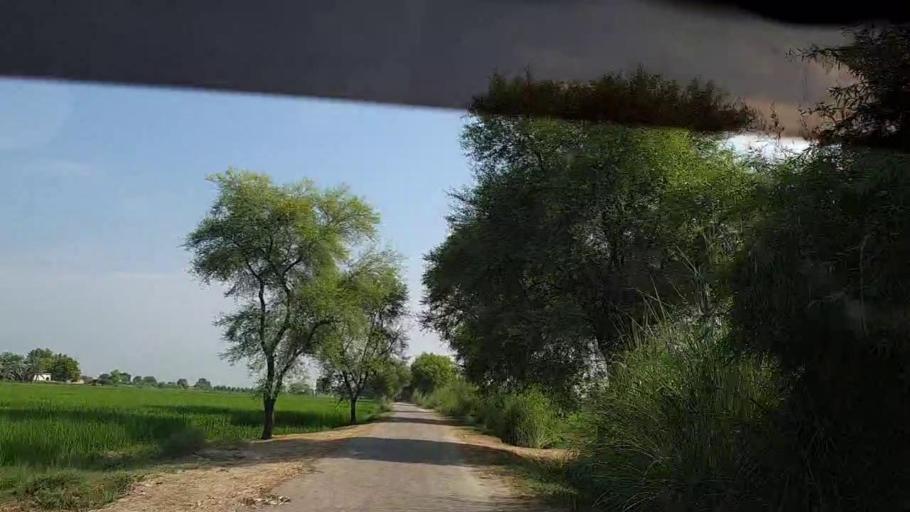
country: PK
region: Sindh
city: Shikarpur
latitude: 28.0957
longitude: 68.6752
